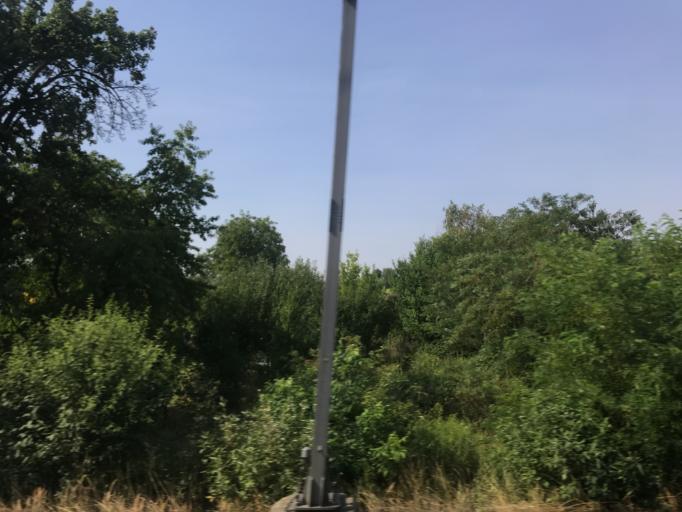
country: CZ
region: Central Bohemia
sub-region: Okres Praha-Vychod
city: Ricany
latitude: 50.0228
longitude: 14.6052
